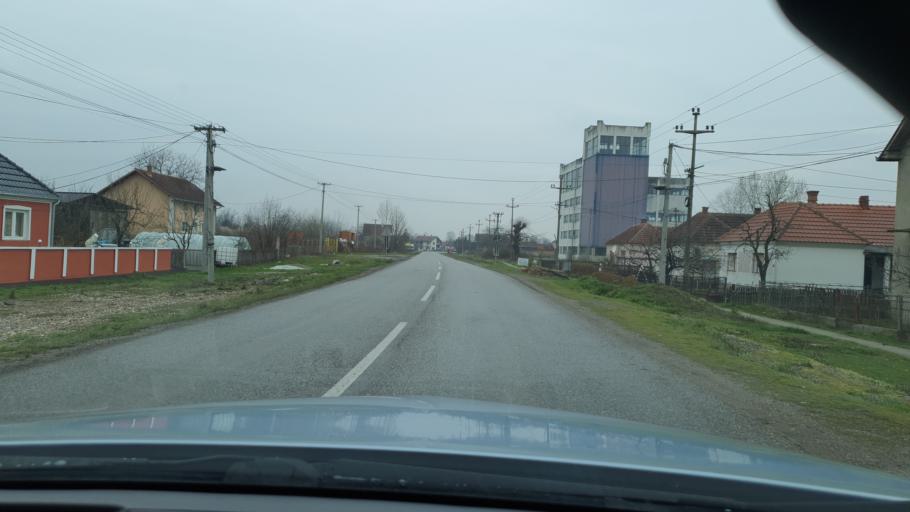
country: RS
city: Stitar
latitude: 44.7821
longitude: 19.6033
